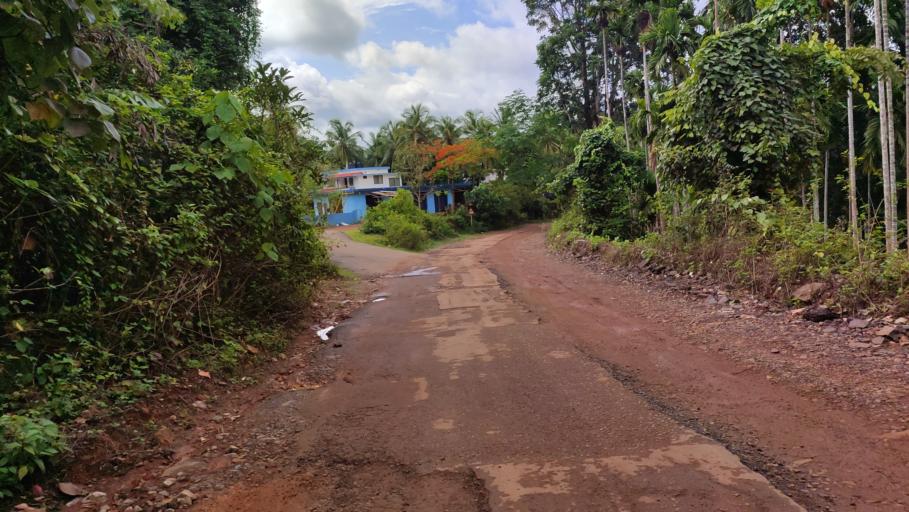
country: IN
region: Kerala
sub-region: Kasaragod District
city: Kasaragod
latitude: 12.5260
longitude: 75.0713
